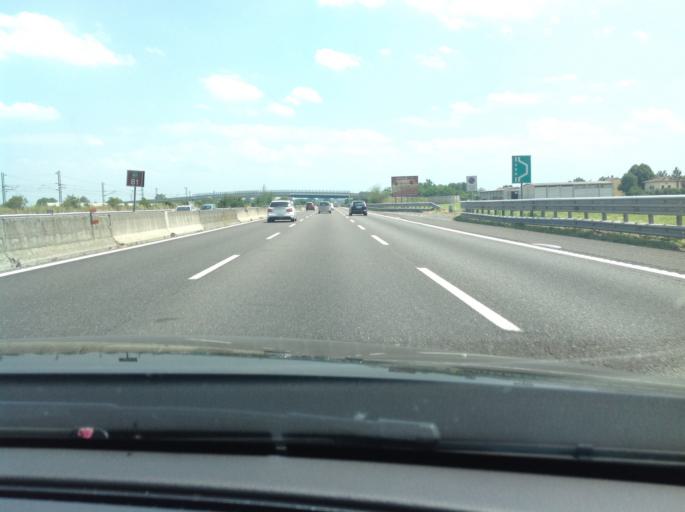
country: IT
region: Emilia-Romagna
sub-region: Provincia di Piacenza
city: Fiorenzuola d'Arda
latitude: 44.9423
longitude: 9.9531
